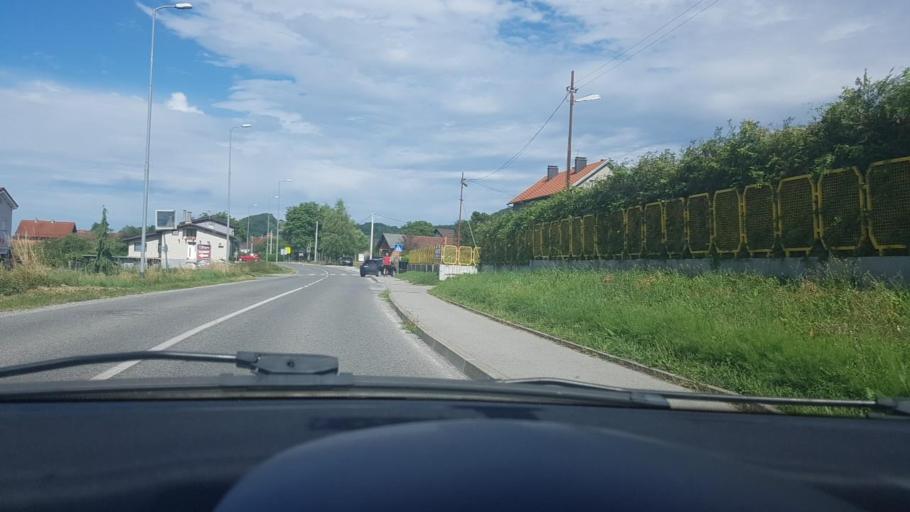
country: HR
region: Varazdinska
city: Lepoglava
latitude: 46.2080
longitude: 16.0512
